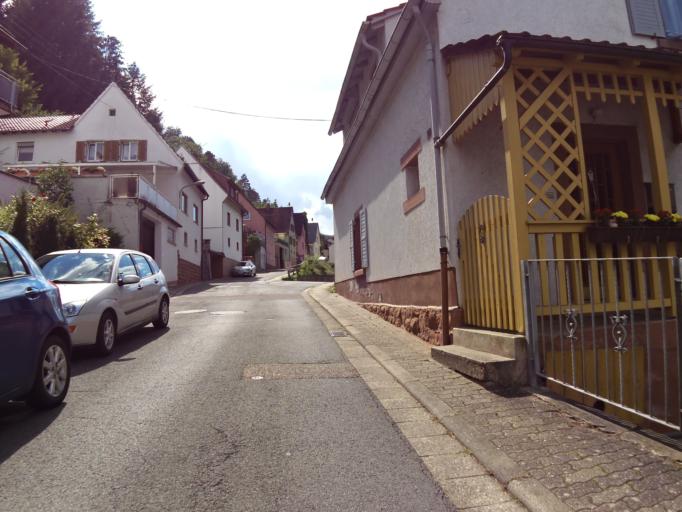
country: DE
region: Rheinland-Pfalz
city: Weidenthal
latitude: 49.4135
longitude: 7.9995
